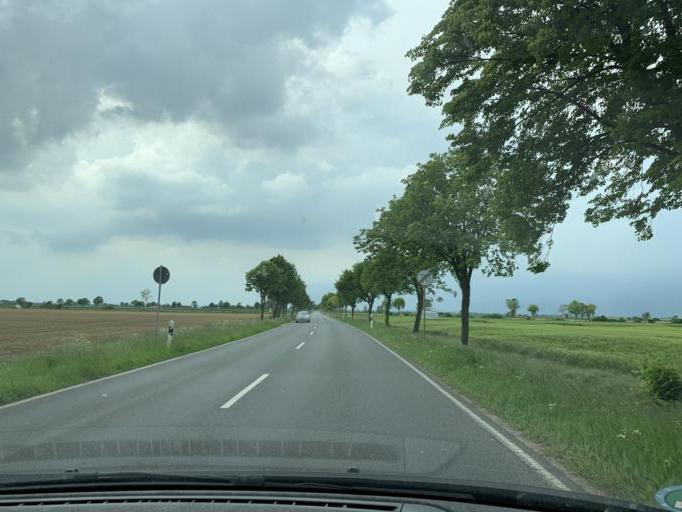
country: DE
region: North Rhine-Westphalia
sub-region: Regierungsbezirk Koln
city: Vettweiss
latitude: 50.7419
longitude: 6.5872
